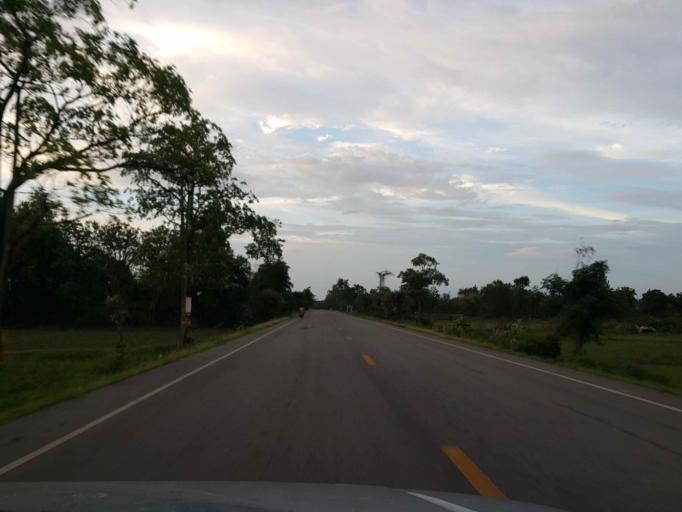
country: TH
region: Sukhothai
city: Ban Dan Lan Hoi
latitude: 17.0625
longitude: 99.5914
